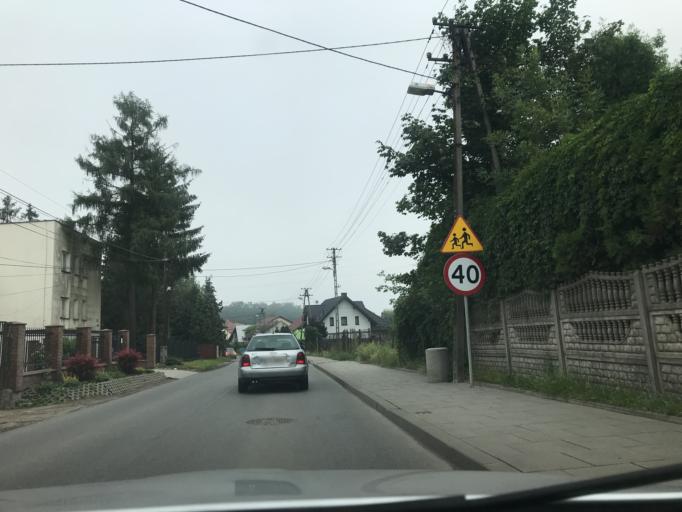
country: PL
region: Lesser Poland Voivodeship
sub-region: Powiat krakowski
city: Ochojno
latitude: 50.0049
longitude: 19.9863
